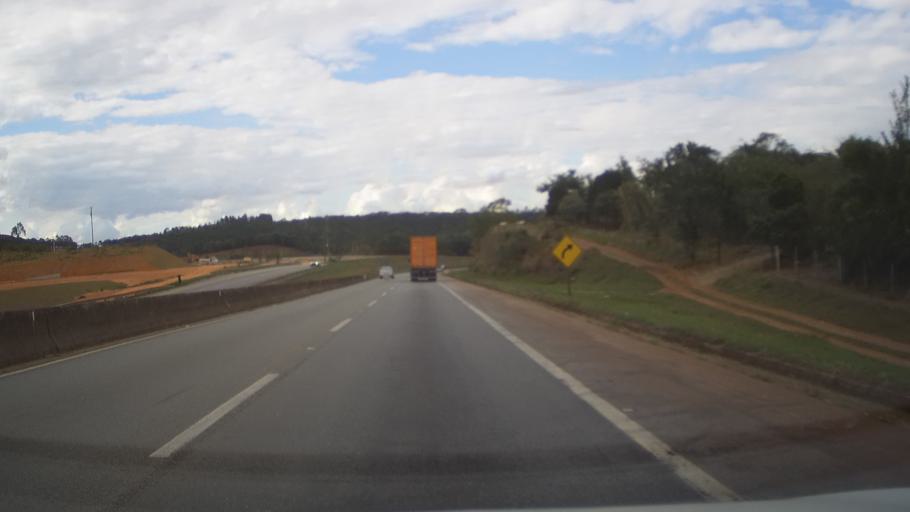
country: BR
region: Minas Gerais
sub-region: Itauna
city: Itauna
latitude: -20.2886
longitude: -44.4357
